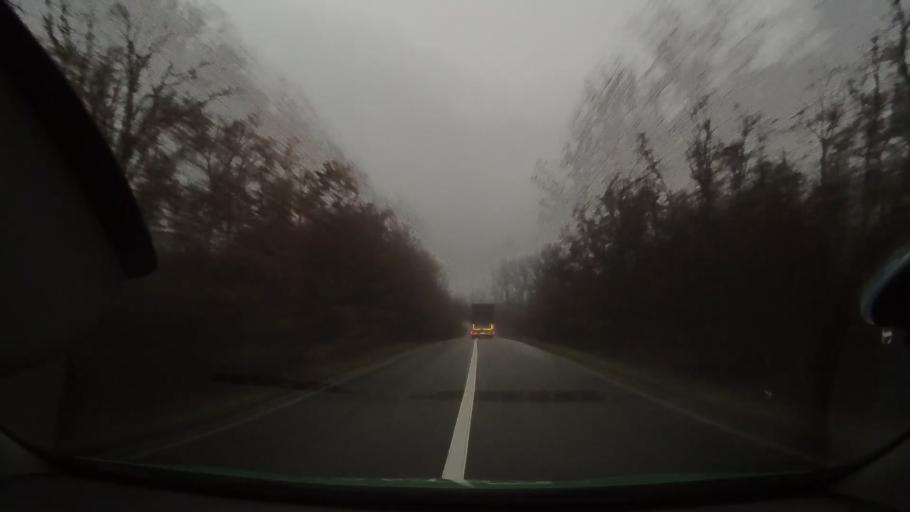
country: RO
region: Arad
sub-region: Comuna Beliu
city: Beliu
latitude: 46.5126
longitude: 21.9606
